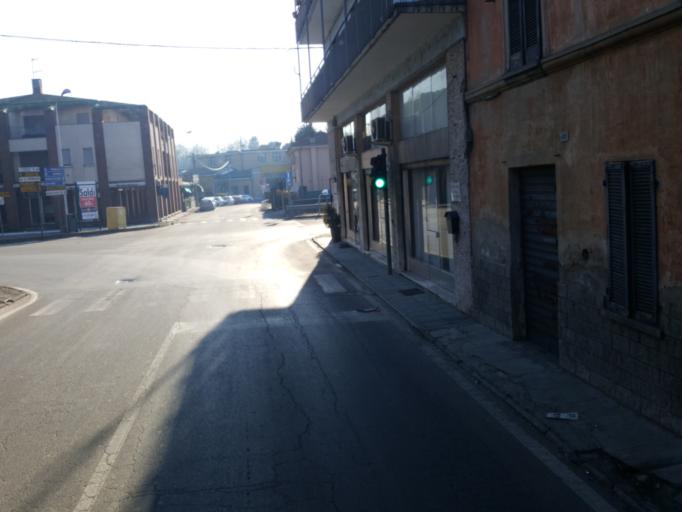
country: IT
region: Piedmont
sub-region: Provincia di Novara
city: Castelletto Sopra Ticino
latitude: 45.7134
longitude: 8.6388
